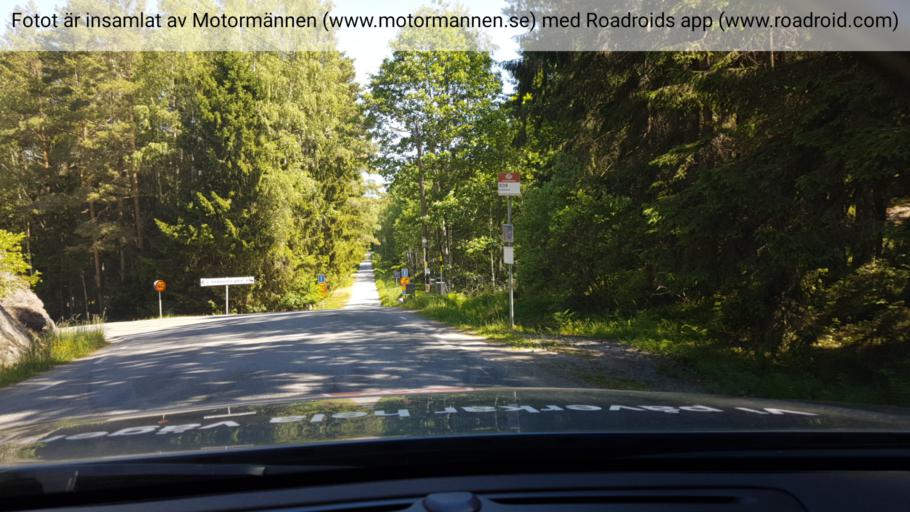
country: SE
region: Stockholm
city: Dalaro
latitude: 59.1542
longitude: 18.4372
